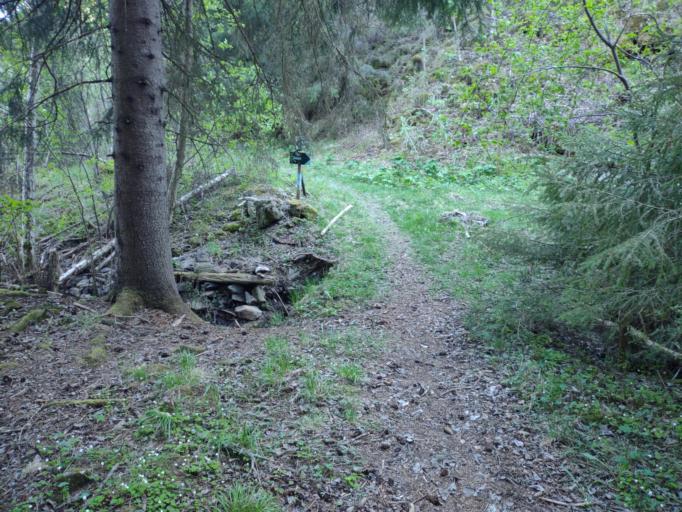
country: NO
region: Oppland
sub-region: Gran
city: Jaren
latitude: 60.4704
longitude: 10.5086
